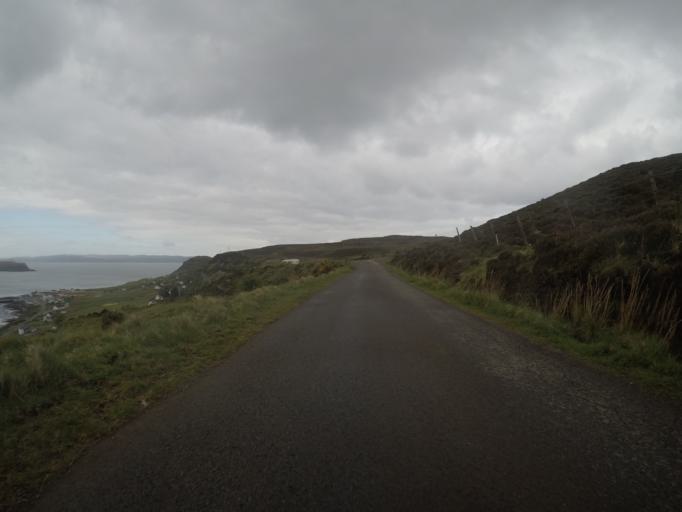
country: GB
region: Scotland
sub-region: Highland
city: Portree
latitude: 57.5937
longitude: -6.3695
